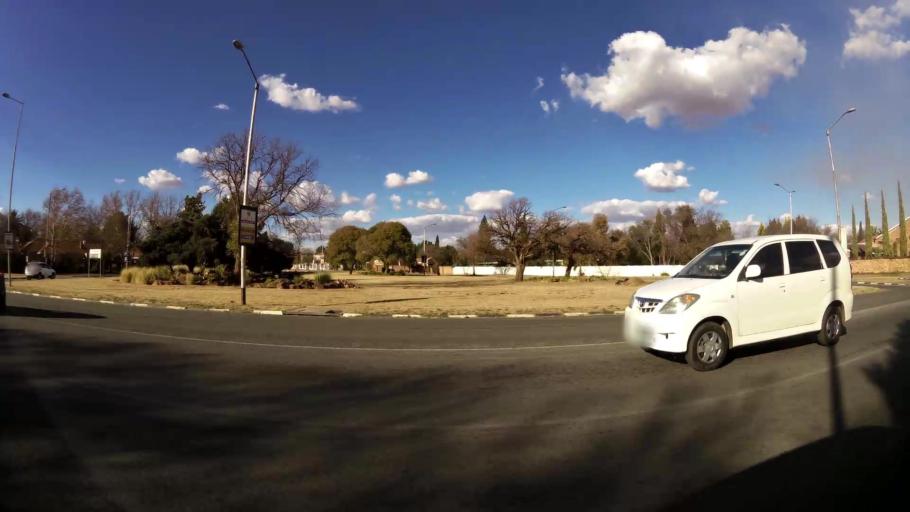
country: ZA
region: North-West
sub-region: Dr Kenneth Kaunda District Municipality
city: Klerksdorp
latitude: -26.8505
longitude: 26.6638
